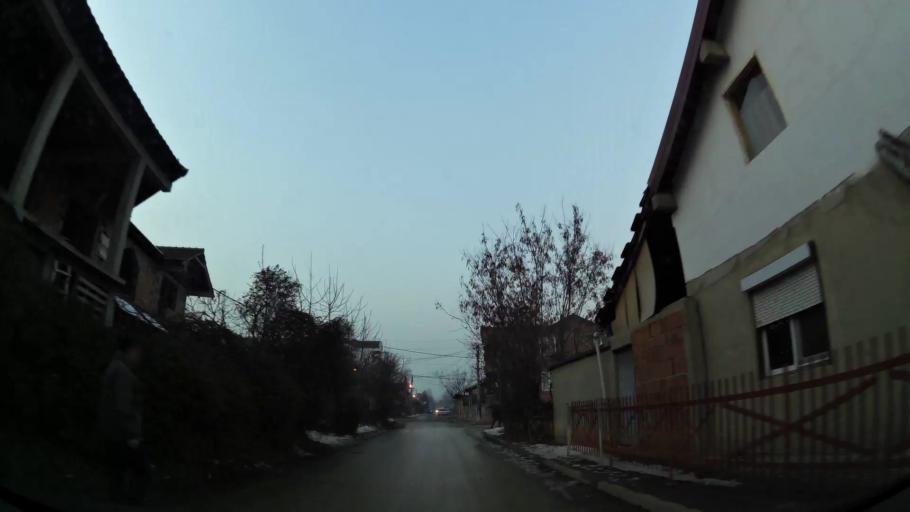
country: MK
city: Creshevo
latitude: 42.0107
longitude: 21.5170
